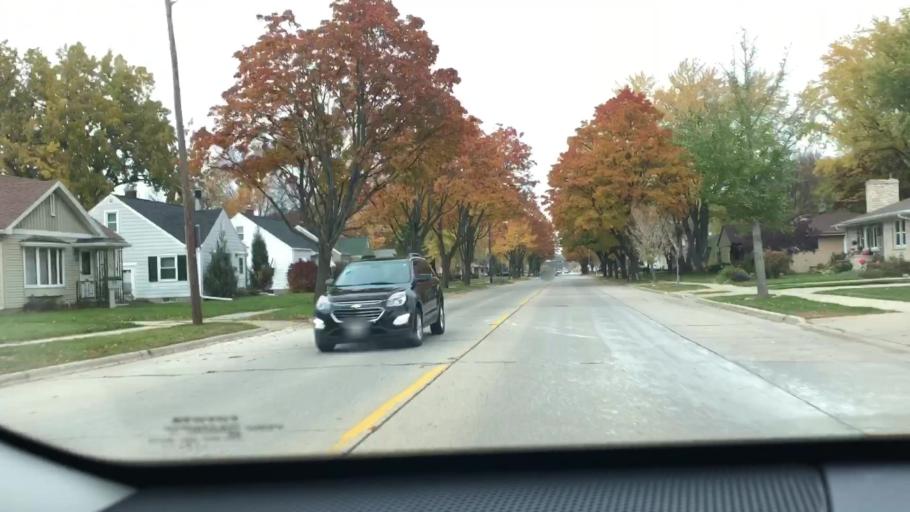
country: US
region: Wisconsin
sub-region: Brown County
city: Green Bay
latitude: 44.5140
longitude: -88.0485
